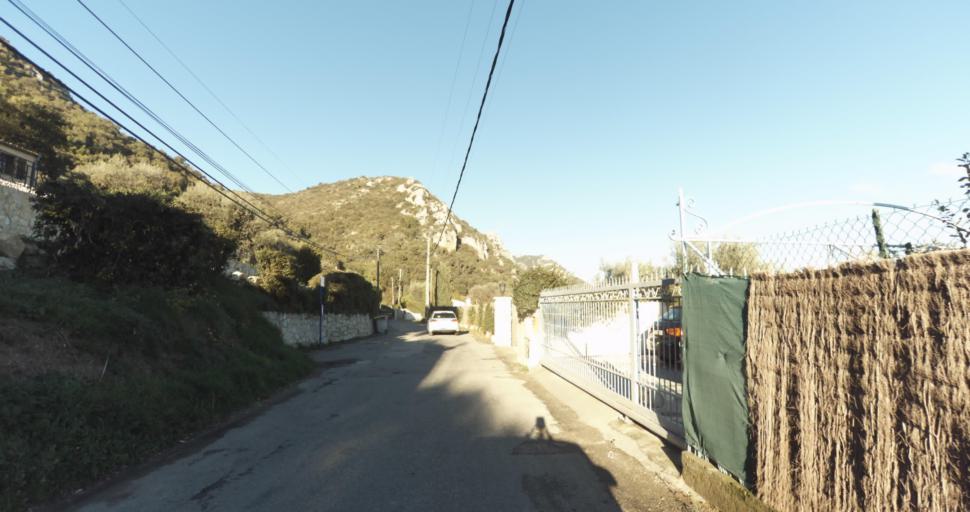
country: FR
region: Provence-Alpes-Cote d'Azur
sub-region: Departement des Alpes-Maritimes
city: Vence
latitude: 43.7355
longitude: 7.1192
